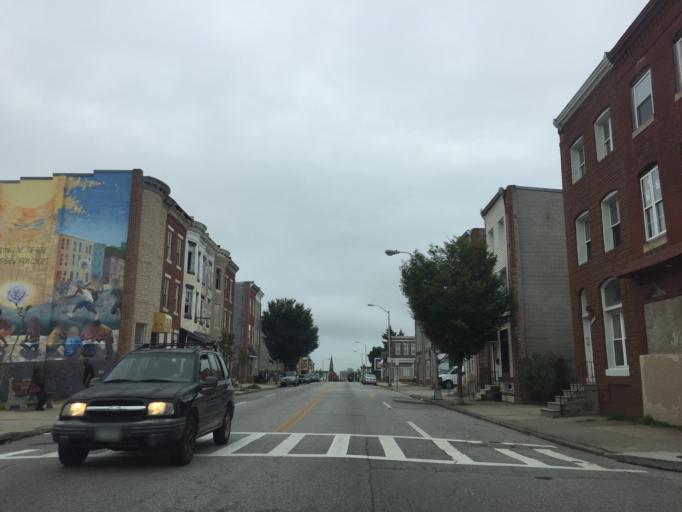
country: US
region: Maryland
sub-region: City of Baltimore
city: Baltimore
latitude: 39.3211
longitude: -76.6095
